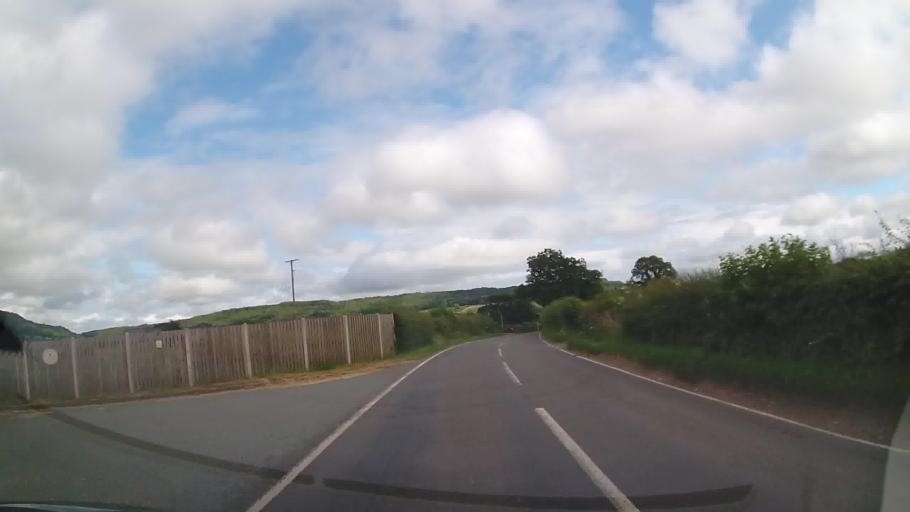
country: GB
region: England
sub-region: Shropshire
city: Pant
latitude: 52.8003
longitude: -3.1234
